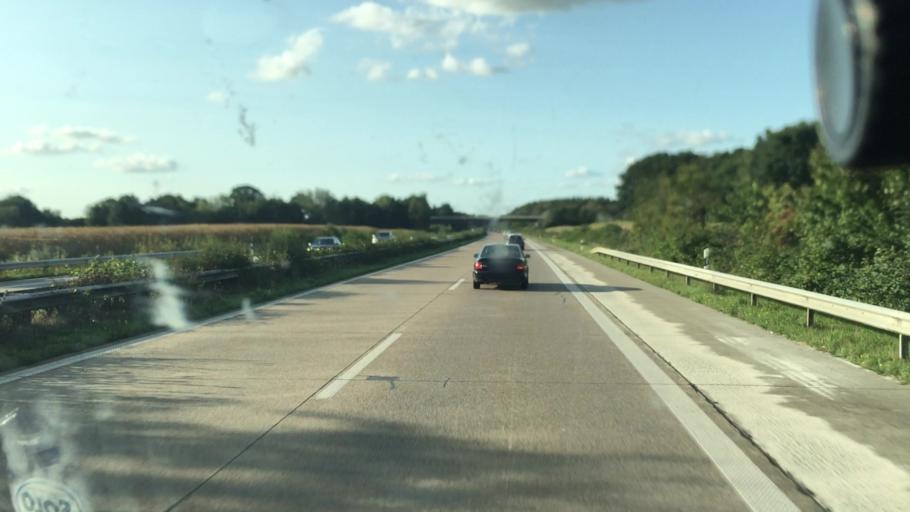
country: DE
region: Lower Saxony
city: Rastede
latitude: 53.2575
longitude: 8.1705
